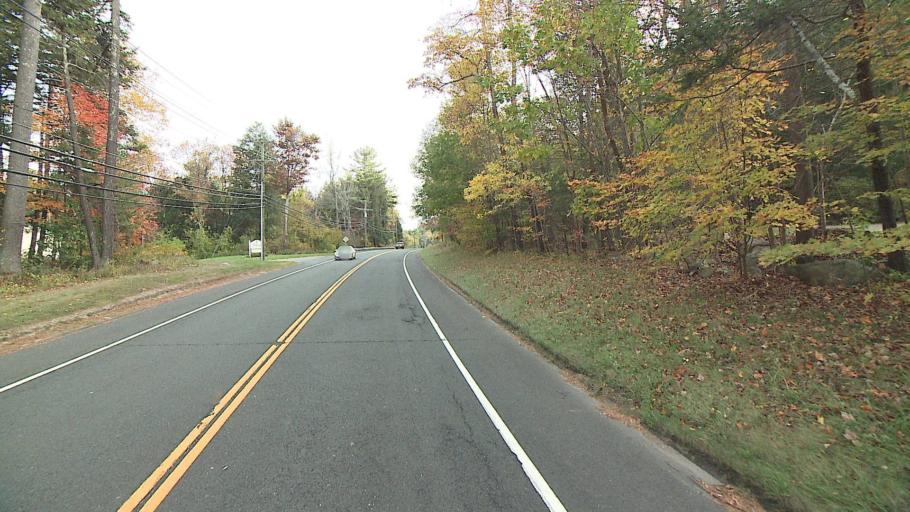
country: US
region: Connecticut
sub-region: Litchfield County
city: New Hartford Center
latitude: 41.9005
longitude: -72.9927
